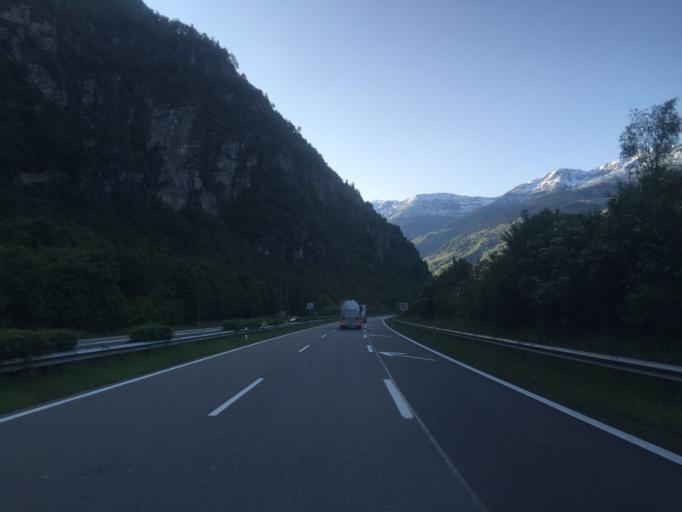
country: CH
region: Ticino
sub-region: Leventina District
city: Faido
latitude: 46.4434
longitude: 8.8334
